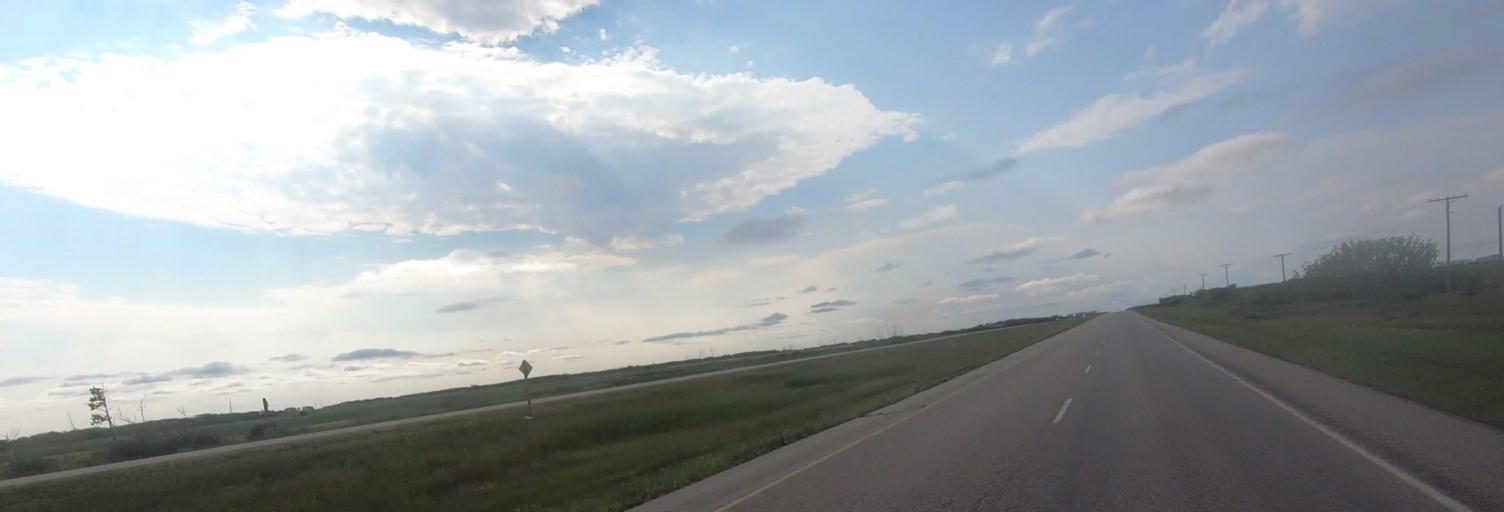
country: CA
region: Saskatchewan
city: Moosomin
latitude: 50.2200
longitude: -101.8227
